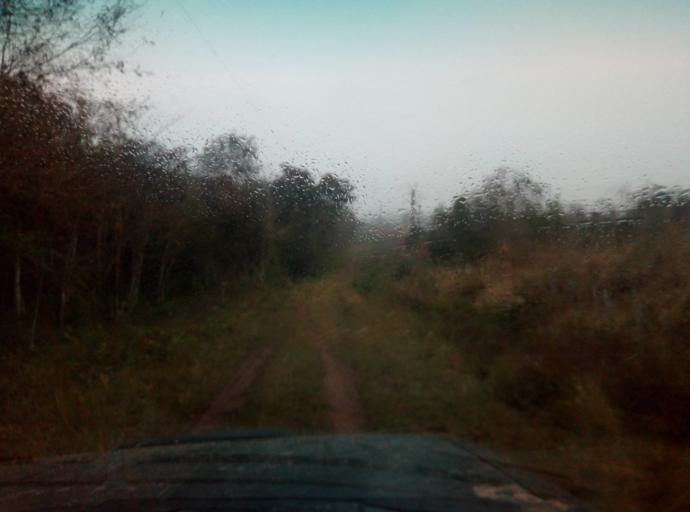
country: PY
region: Caaguazu
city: Doctor Cecilio Baez
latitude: -25.1519
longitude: -56.2607
